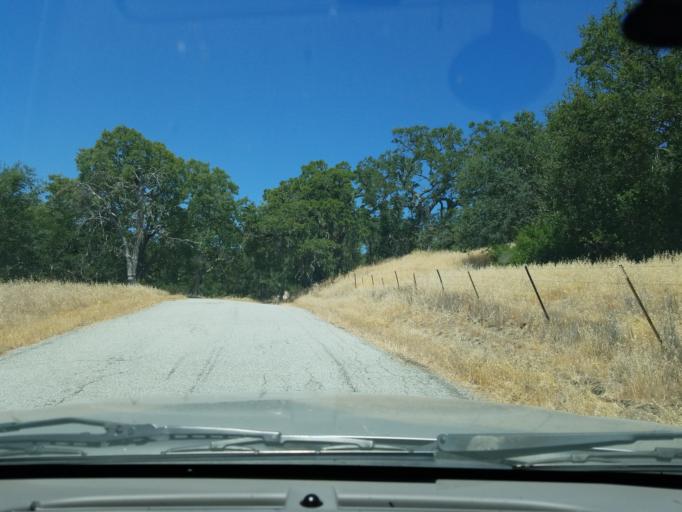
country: US
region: California
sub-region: Monterey County
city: Gonzales
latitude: 36.3407
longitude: -121.5192
